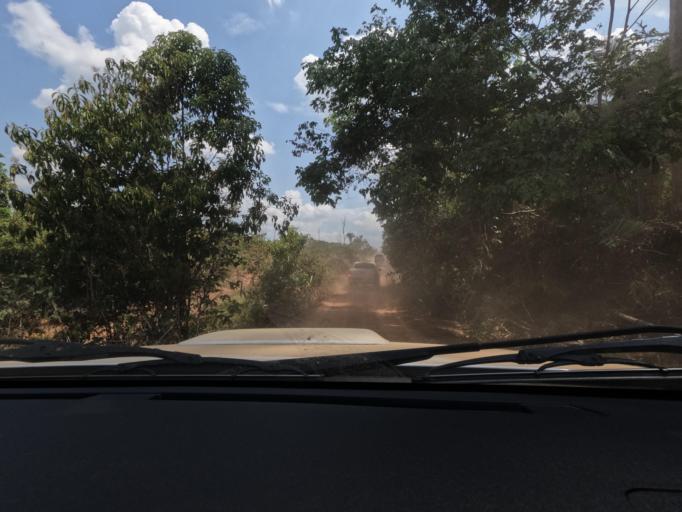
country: BR
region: Rondonia
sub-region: Porto Velho
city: Porto Velho
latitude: -8.6060
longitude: -64.2205
